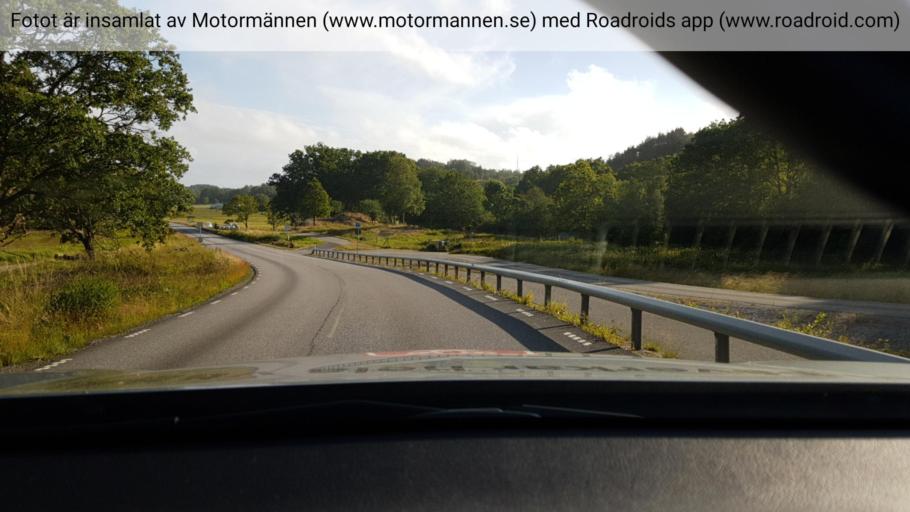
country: SE
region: Vaestra Goetaland
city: Svanesund
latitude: 58.1228
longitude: 11.8569
